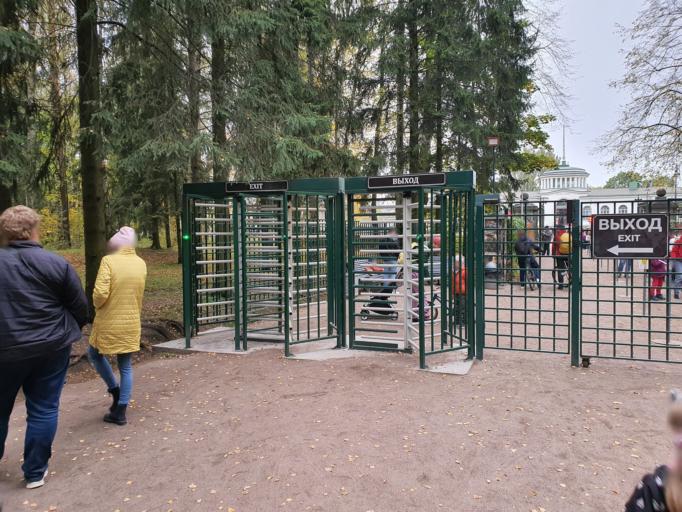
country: RU
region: St.-Petersburg
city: Pavlovsk
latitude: 59.6927
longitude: 30.4349
